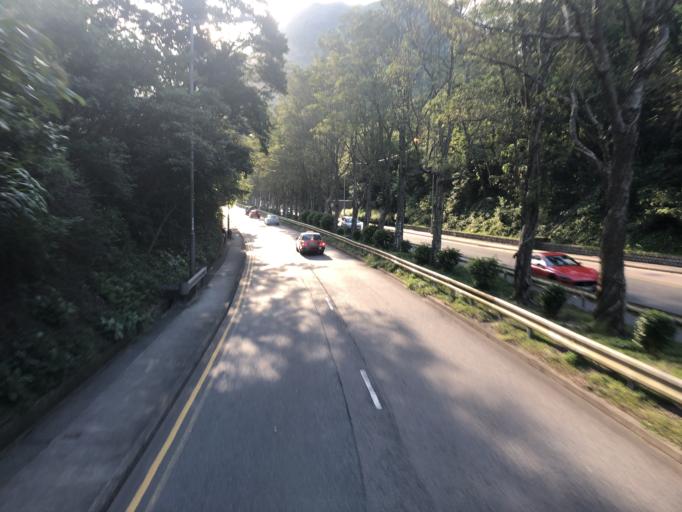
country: HK
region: Wong Tai Sin
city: Wong Tai Sin
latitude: 22.3337
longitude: 114.2329
